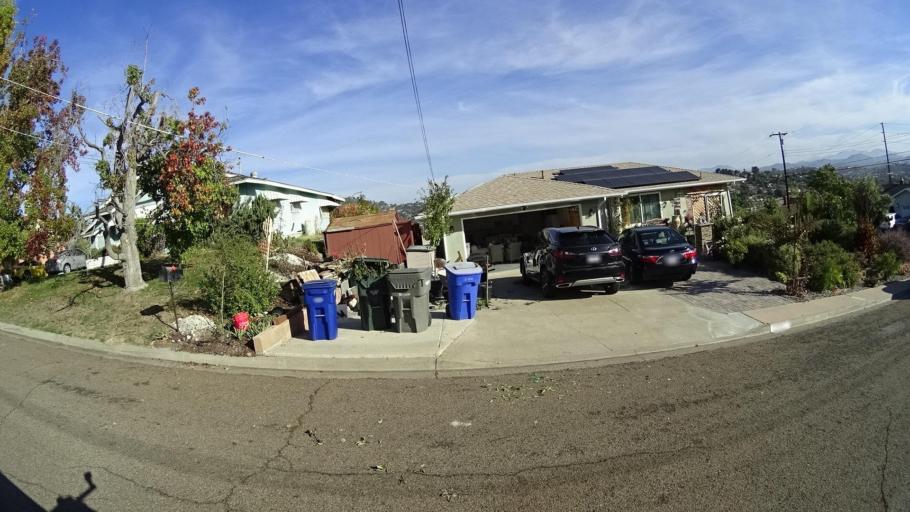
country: US
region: California
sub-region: San Diego County
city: Spring Valley
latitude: 32.7392
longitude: -116.9763
